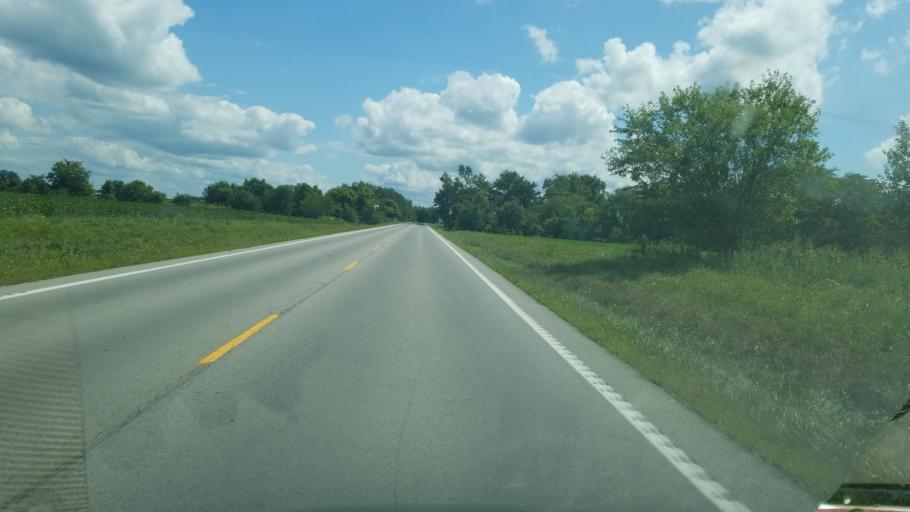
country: US
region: Ohio
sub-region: Putnam County
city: Kalida
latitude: 40.9439
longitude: -84.1606
